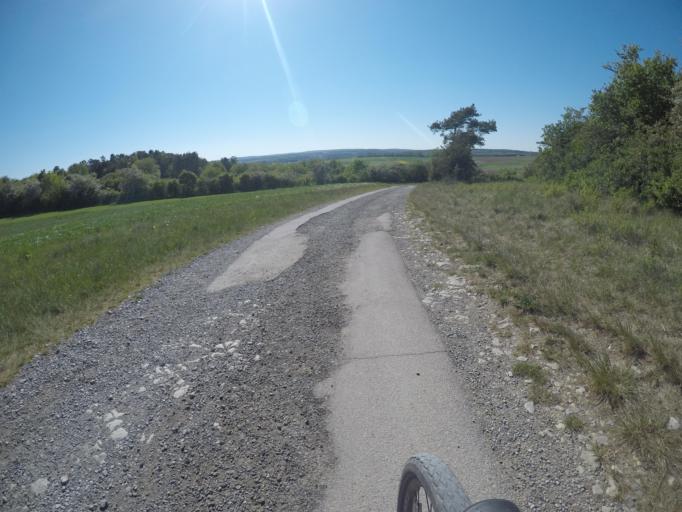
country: DE
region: Baden-Wuerttemberg
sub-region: Karlsruhe Region
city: Friolzheim
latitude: 48.8266
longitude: 8.8439
